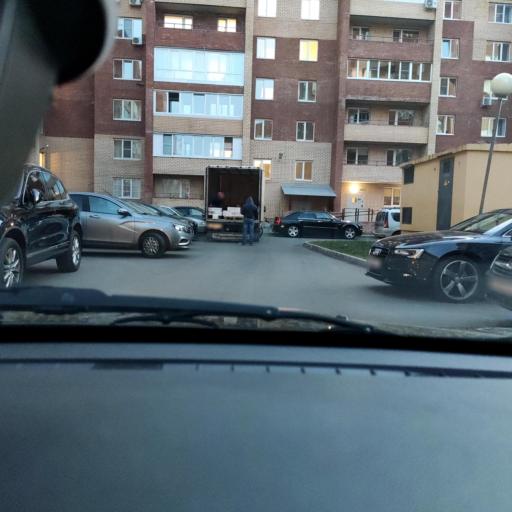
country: RU
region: Samara
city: Tol'yatti
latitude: 53.5352
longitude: 49.3546
